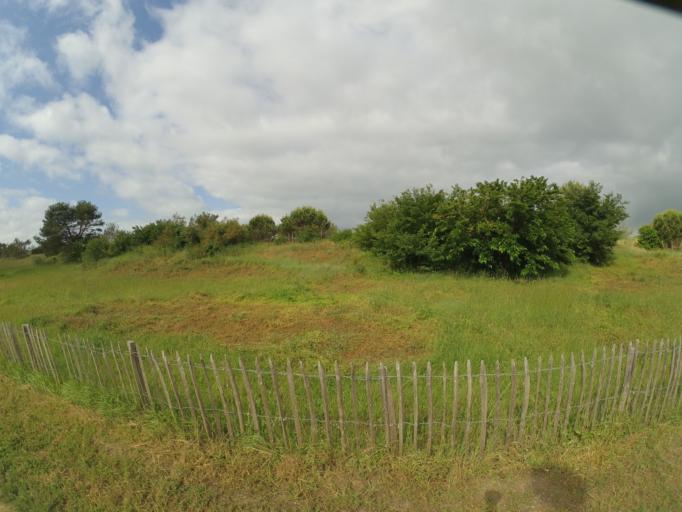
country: FR
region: Poitou-Charentes
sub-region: Departement de la Charente-Maritime
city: Aytre
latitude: 46.1199
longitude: -1.1235
